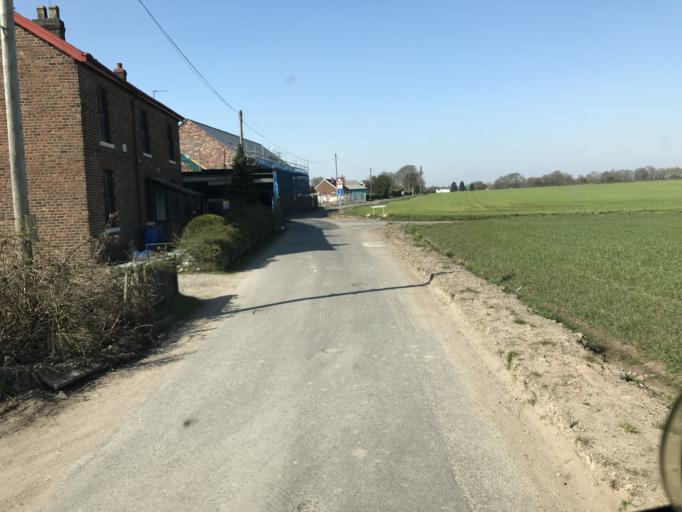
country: GB
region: England
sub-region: Trafford
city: Partington
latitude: 53.4222
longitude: -2.4681
